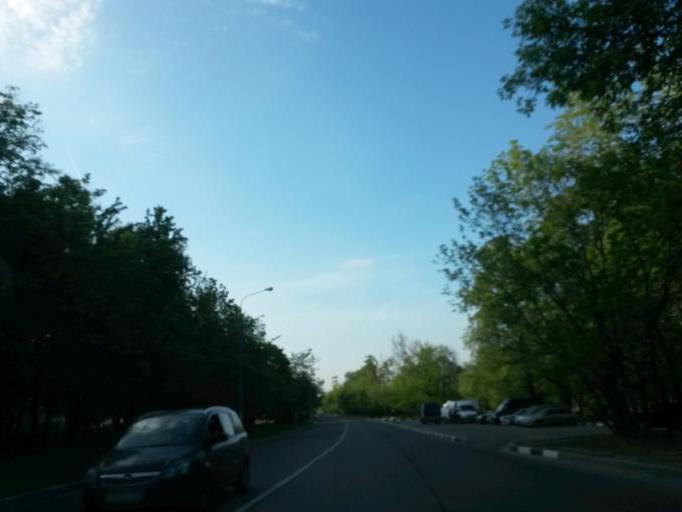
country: RU
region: Moscow
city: Zagor'ye
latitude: 55.5759
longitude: 37.6599
